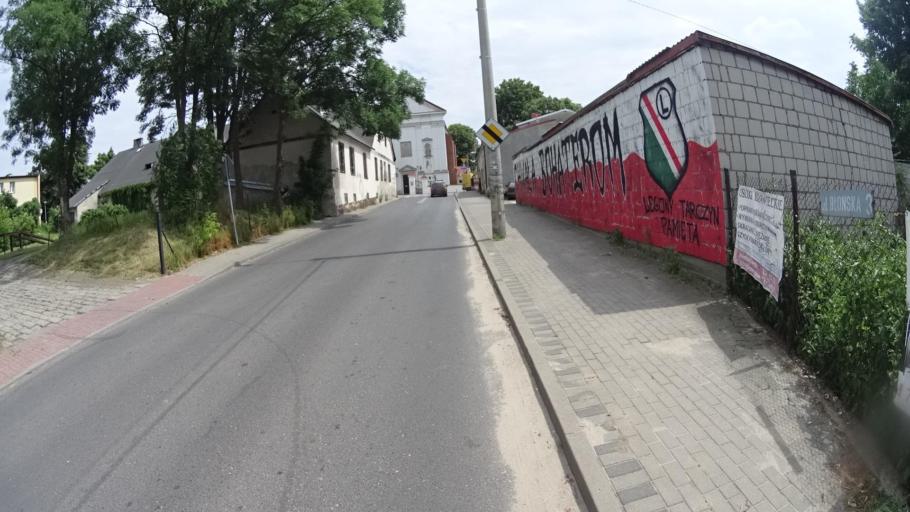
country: PL
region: Masovian Voivodeship
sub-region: Powiat piaseczynski
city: Tarczyn
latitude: 51.9808
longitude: 20.8328
